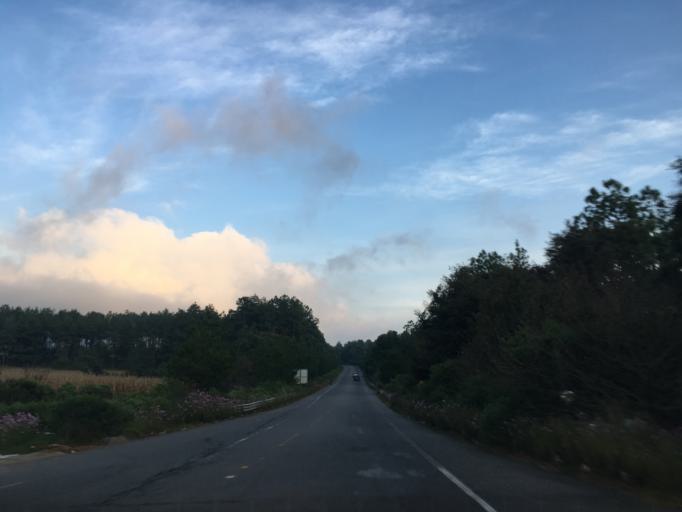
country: MX
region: Michoacan
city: Angahuan
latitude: 19.5703
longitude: -102.2573
